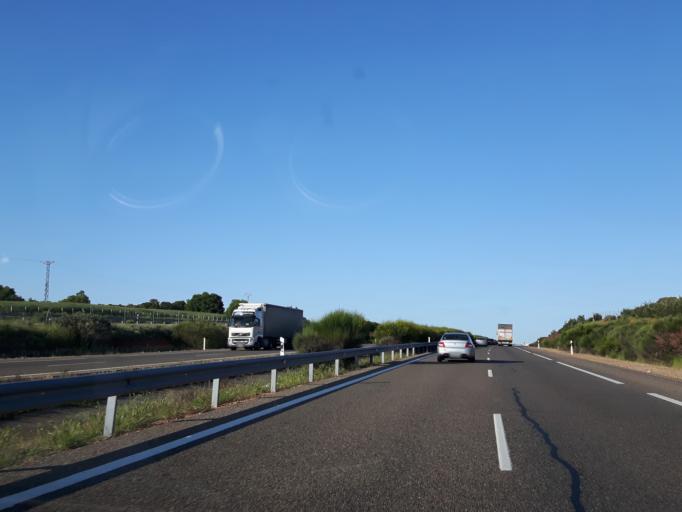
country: ES
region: Castille and Leon
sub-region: Provincia de Salamanca
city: Aldehuela de la Boveda
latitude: 40.8336
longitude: -6.0950
